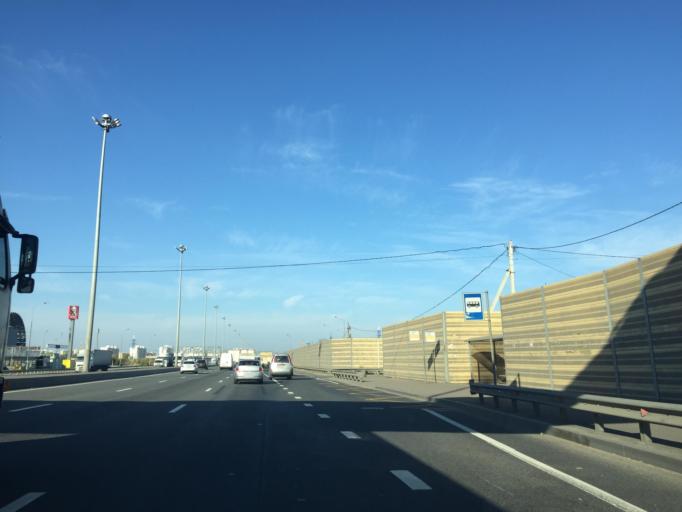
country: RU
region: St.-Petersburg
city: Petro-Slavyanka
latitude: 59.7472
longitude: 30.4998
